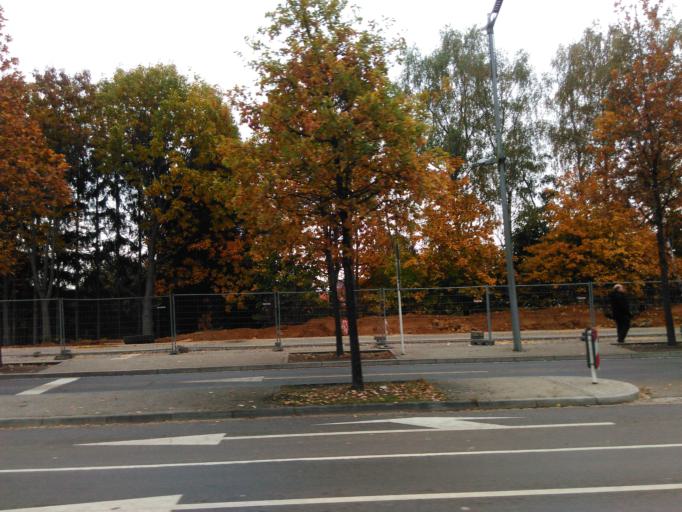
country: LU
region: Luxembourg
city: Kirchberg
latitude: 49.6260
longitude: 6.1612
